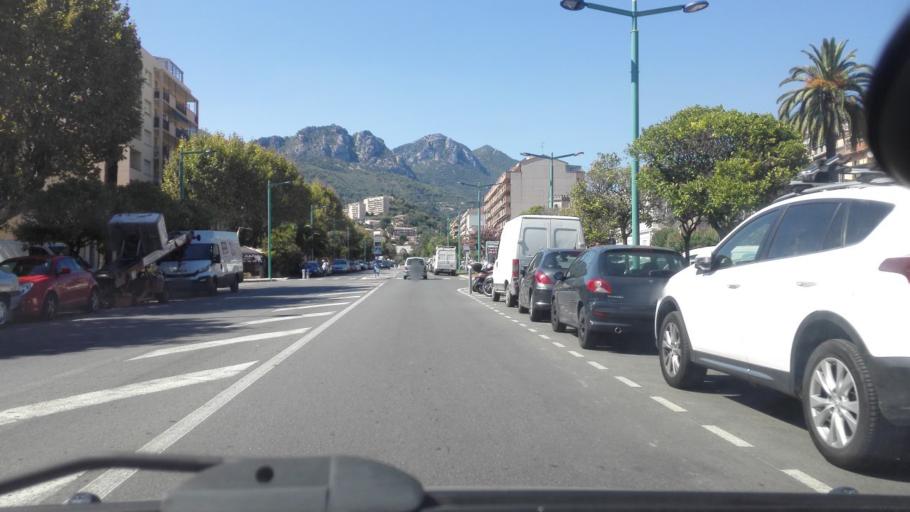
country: FR
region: Provence-Alpes-Cote d'Azur
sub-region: Departement des Alpes-Maritimes
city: Roquebrune-Cap-Martin
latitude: 43.7738
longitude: 7.4900
